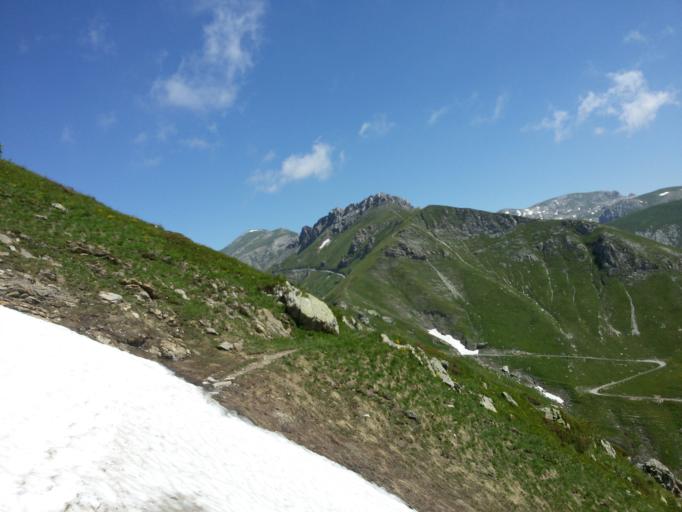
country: IT
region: Piedmont
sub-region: Provincia di Cuneo
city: Limone Piemonte
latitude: 44.1523
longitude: 7.6238
